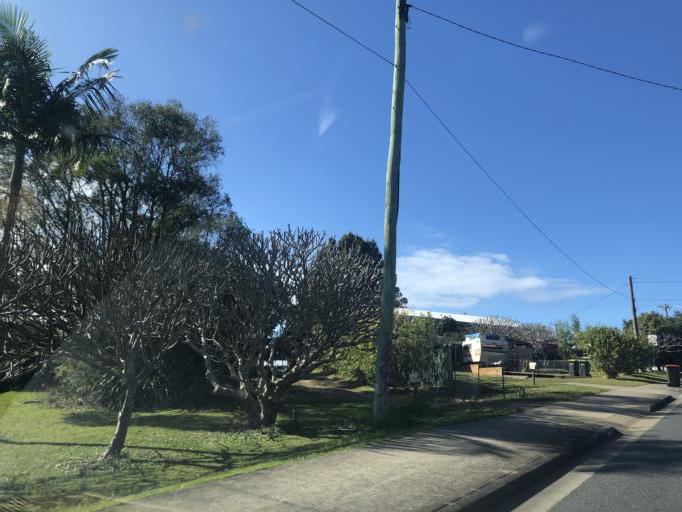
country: AU
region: New South Wales
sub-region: Coffs Harbour
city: Toormina
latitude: -30.3400
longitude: 153.0839
